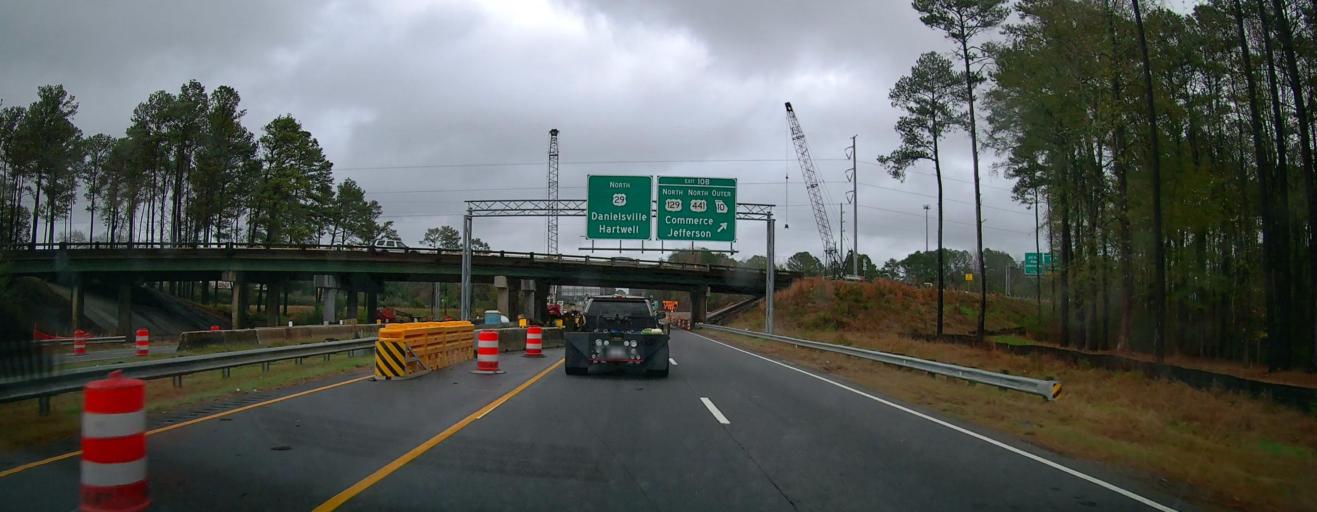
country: US
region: Georgia
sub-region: Clarke County
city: Athens
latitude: 33.9772
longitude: -83.3529
